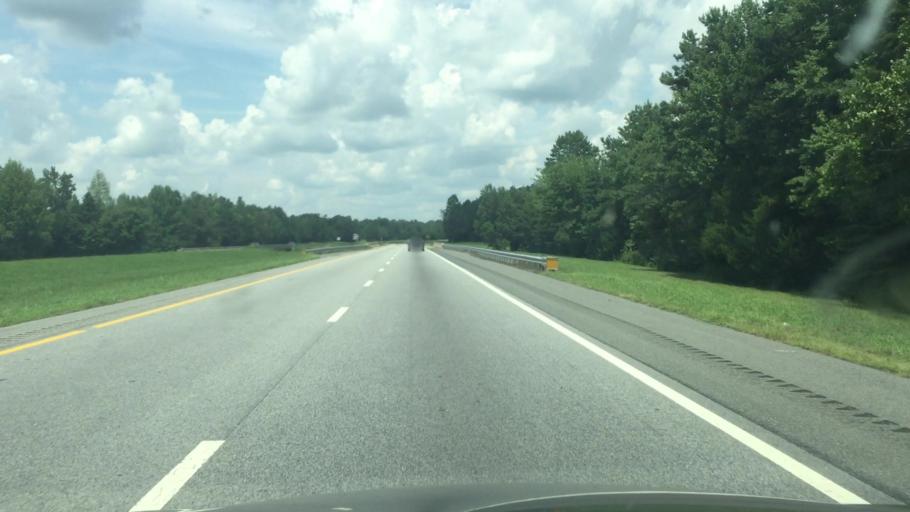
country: US
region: North Carolina
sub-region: Guilford County
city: Pleasant Garden
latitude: 35.9209
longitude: -79.8246
